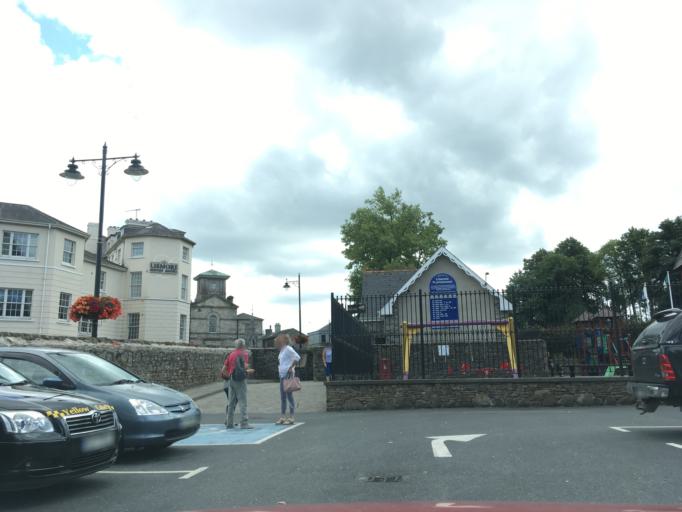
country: IE
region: Munster
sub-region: County Cork
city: Youghal
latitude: 52.1381
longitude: -7.9330
